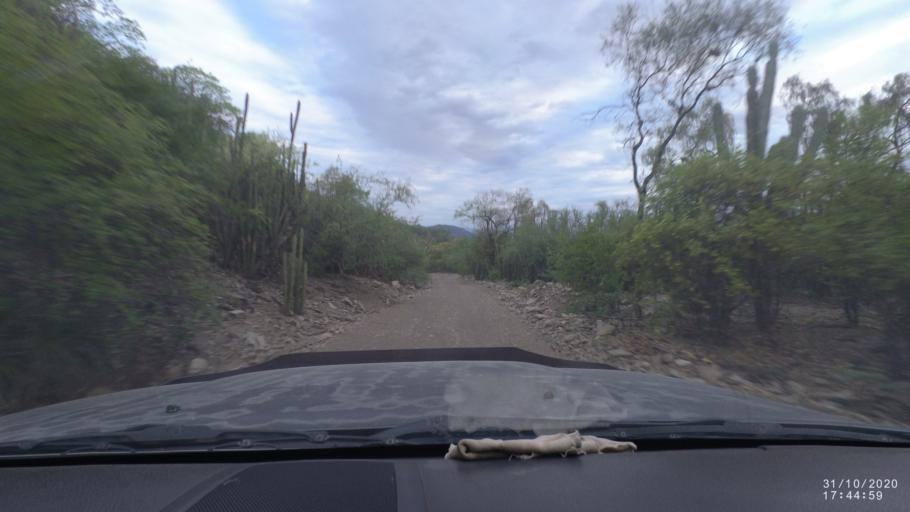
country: BO
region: Chuquisaca
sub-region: Provincia Zudanez
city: Mojocoya
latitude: -18.6129
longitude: -64.5448
